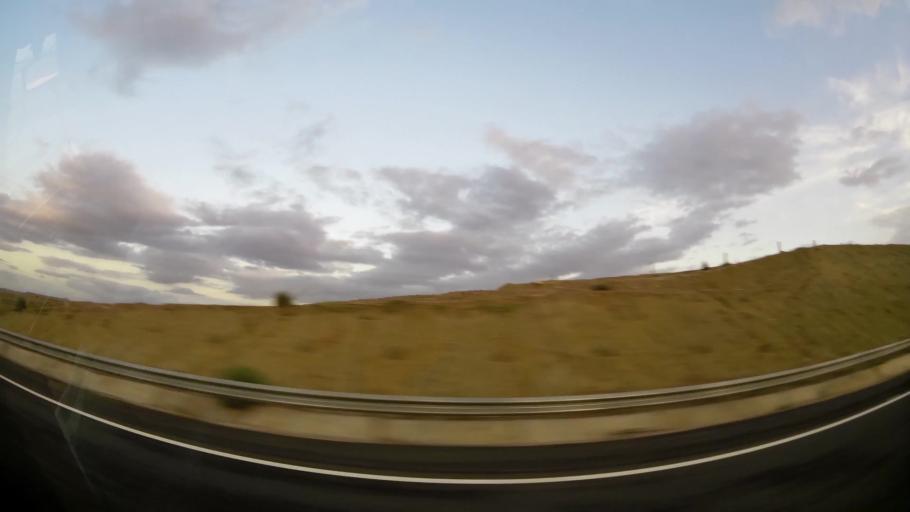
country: MA
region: Oriental
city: Taourirt
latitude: 34.5674
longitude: -2.8294
